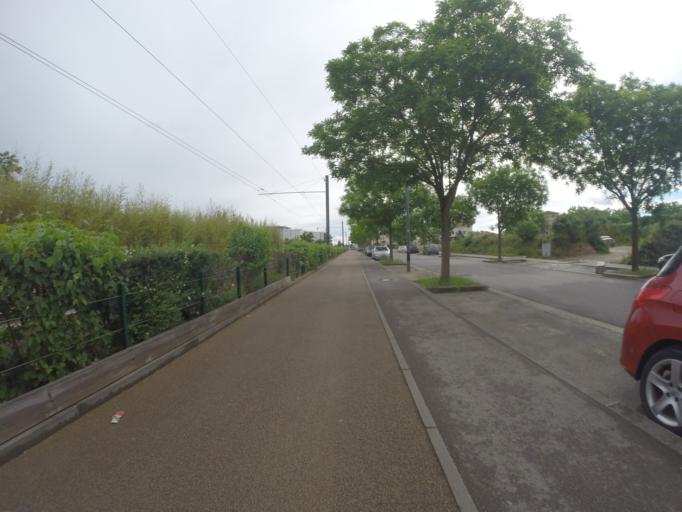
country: FR
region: Rhone-Alpes
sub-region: Departement du Rhone
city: Vaulx-en-Velin
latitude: 45.7622
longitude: 4.9275
